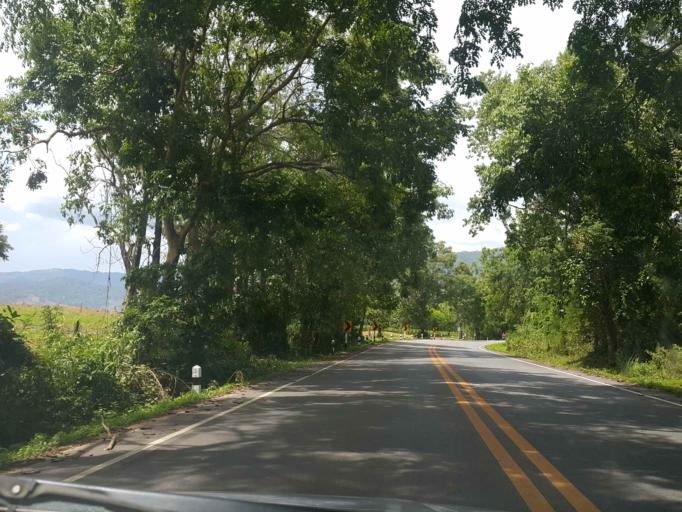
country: TH
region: Nan
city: Ban Luang
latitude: 18.8633
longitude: 100.4641
